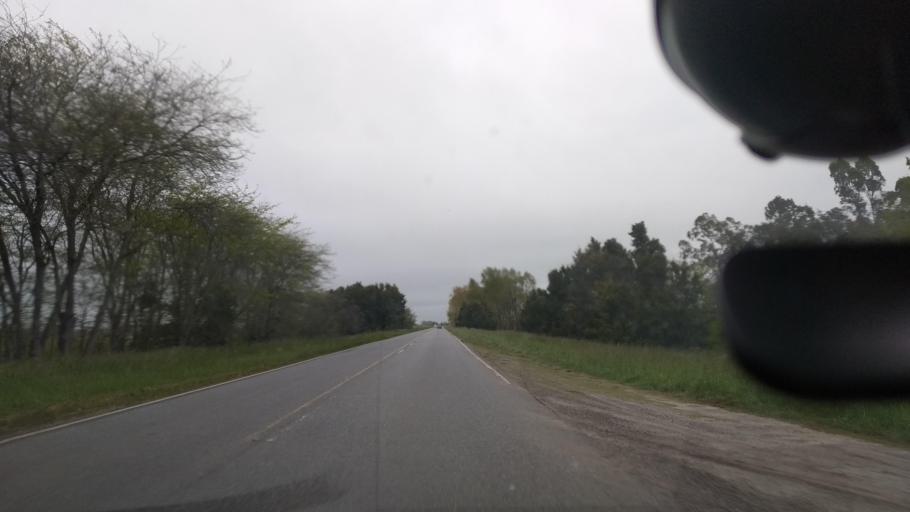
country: AR
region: Buenos Aires
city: Veronica
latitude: -35.3079
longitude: -57.4944
